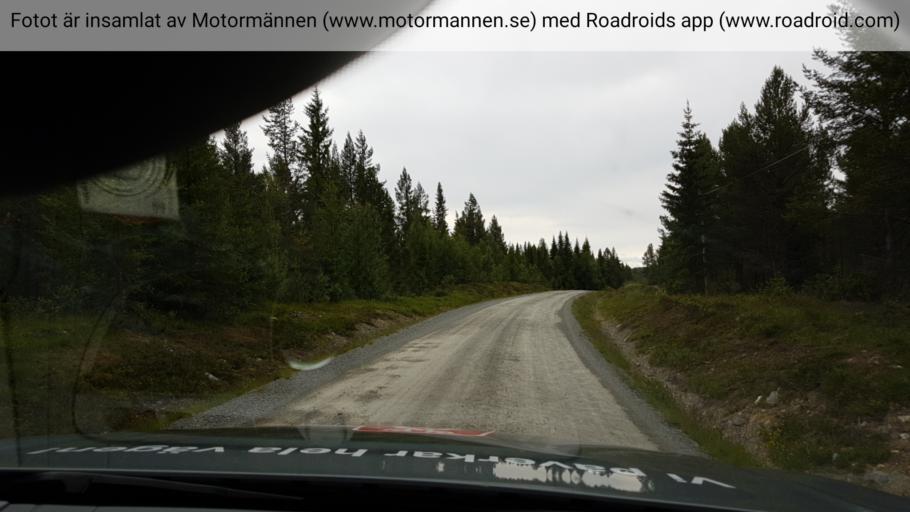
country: SE
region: Jaemtland
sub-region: Are Kommun
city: Jarpen
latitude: 62.8279
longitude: 13.8198
